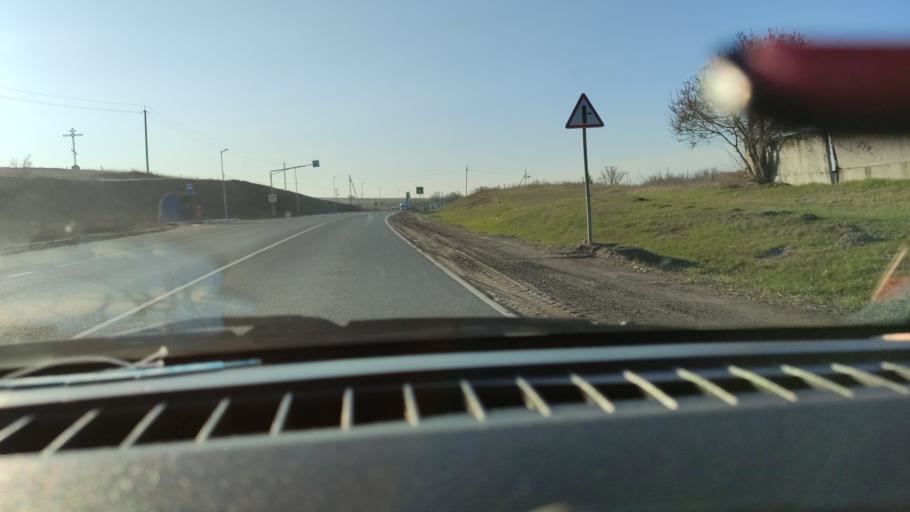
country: RU
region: Saratov
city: Tersa
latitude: 52.0955
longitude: 47.5387
